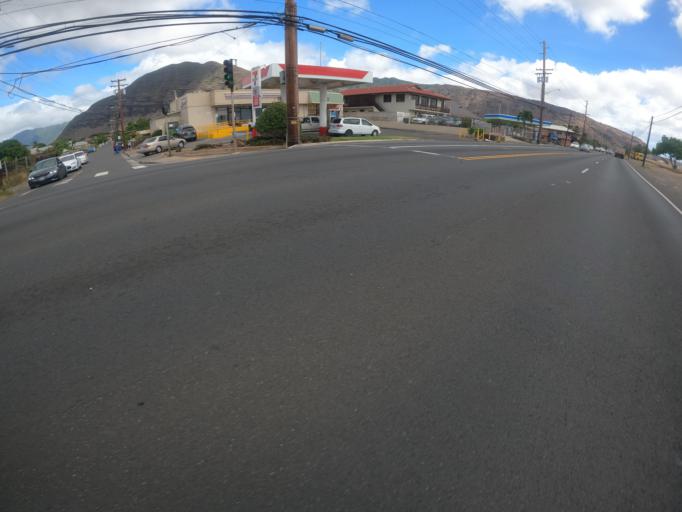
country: US
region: Hawaii
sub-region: Honolulu County
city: Nanakuli
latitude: 21.3894
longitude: -158.1540
